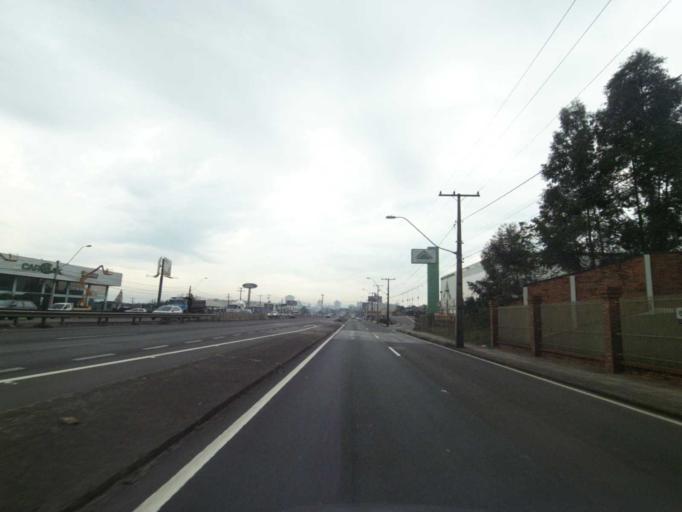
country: BR
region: Rio Grande do Sul
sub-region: Sao Leopoldo
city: Sao Leopoldo
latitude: -29.7811
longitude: -51.1587
